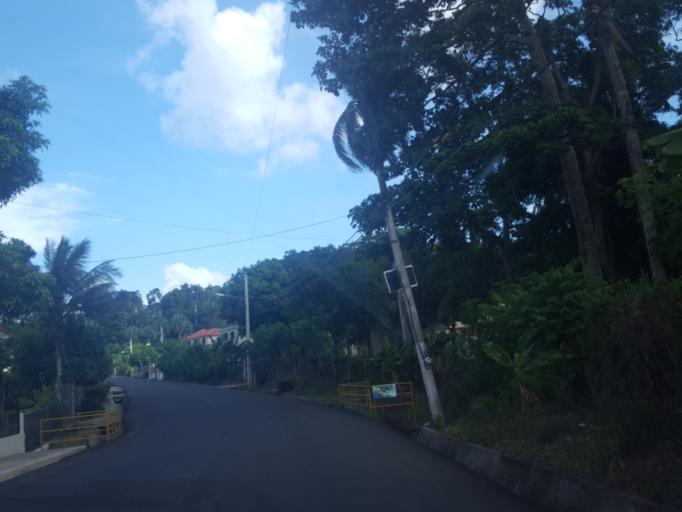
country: DO
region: La Vega
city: Rio Verde Arriba
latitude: 19.3567
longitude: -70.6321
